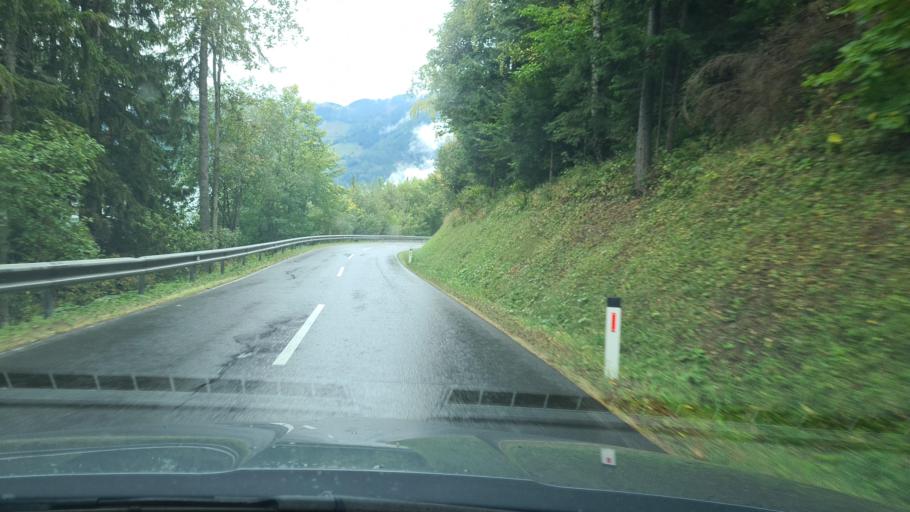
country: AT
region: Styria
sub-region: Politischer Bezirk Weiz
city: Gasen
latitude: 47.3676
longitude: 15.4736
